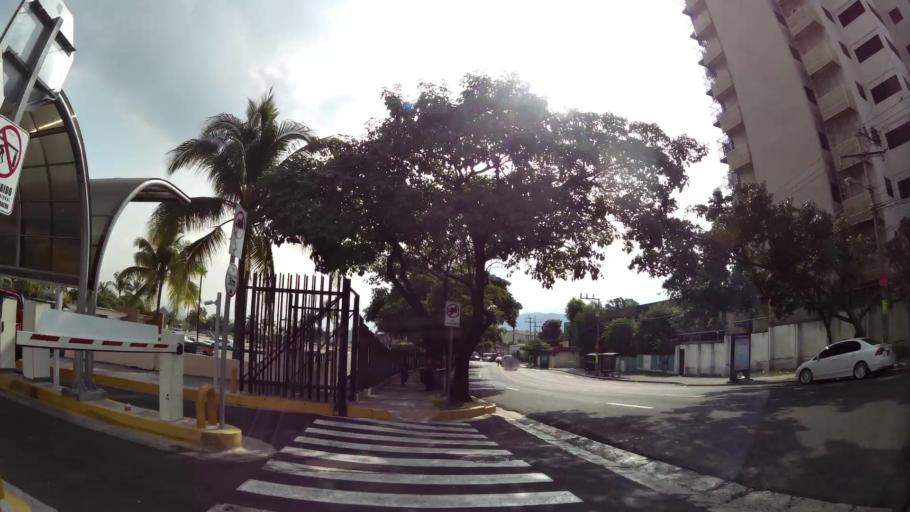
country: SV
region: San Salvador
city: San Salvador
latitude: 13.7046
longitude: -89.2097
